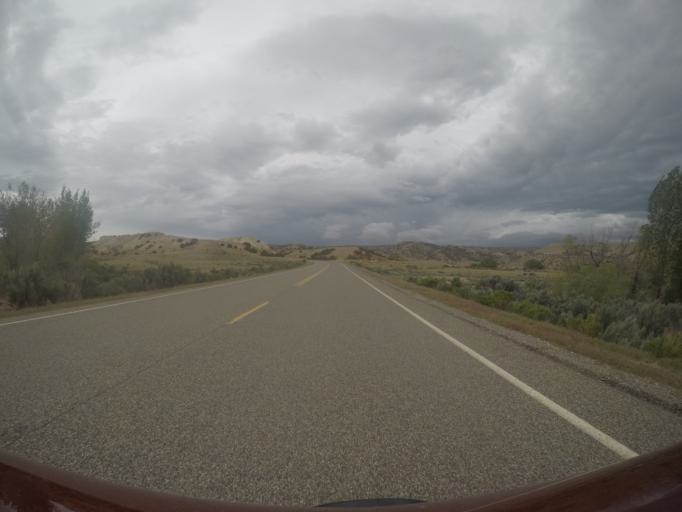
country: US
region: Wyoming
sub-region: Big Horn County
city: Lovell
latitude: 44.9702
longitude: -108.2662
